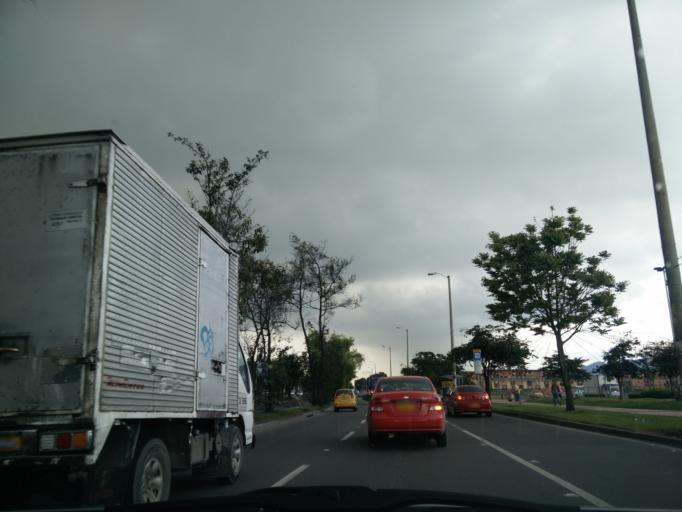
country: CO
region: Cundinamarca
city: Cota
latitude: 4.7477
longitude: -74.0977
